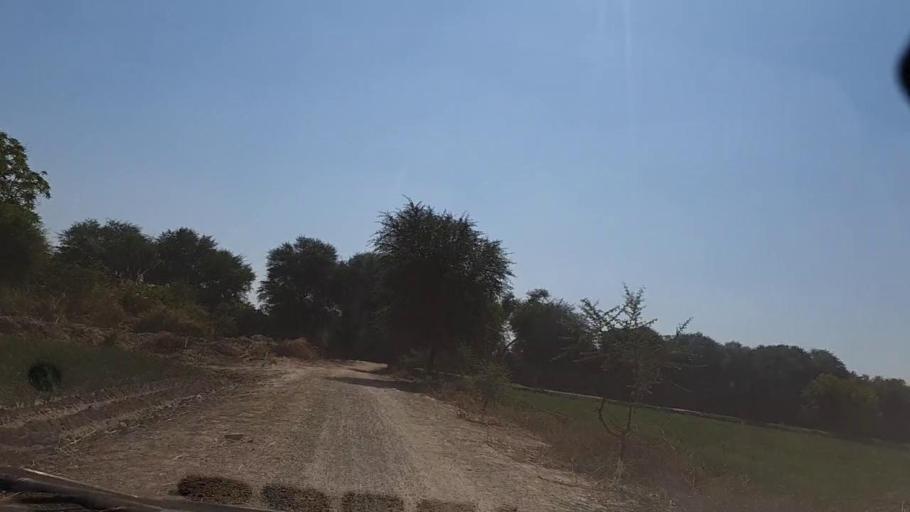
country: PK
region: Sindh
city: Mirpur Khas
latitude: 25.4265
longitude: 69.0559
